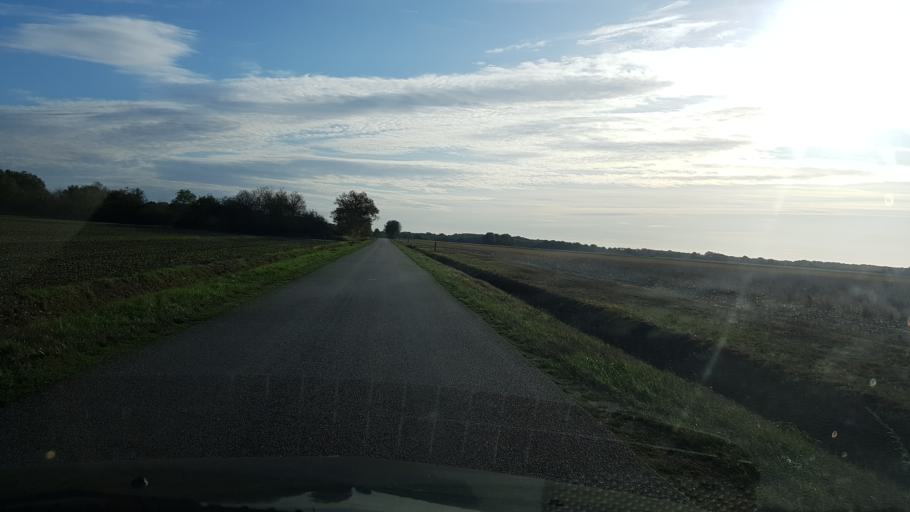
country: FR
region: Centre
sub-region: Departement du Loiret
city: Cerdon
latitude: 47.6707
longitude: 2.2891
